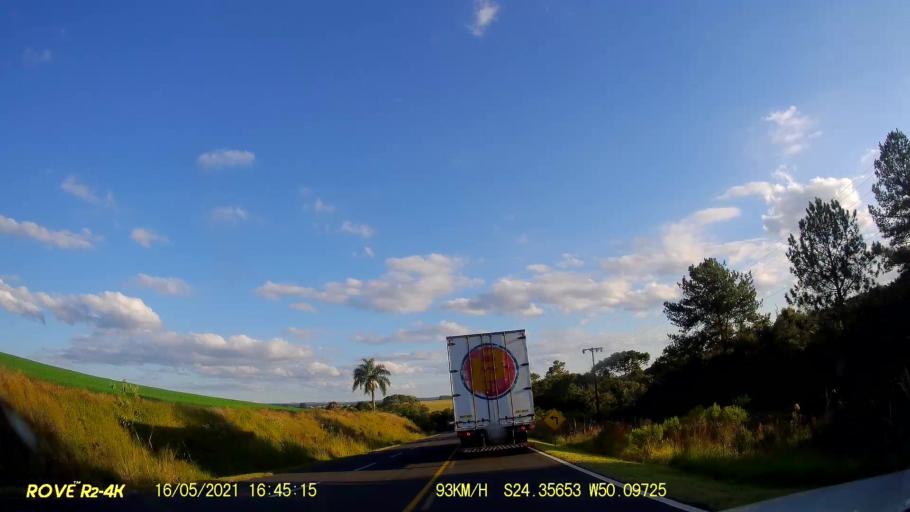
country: BR
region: Parana
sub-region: Pirai Do Sul
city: Pirai do Sul
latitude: -24.3530
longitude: -50.0977
